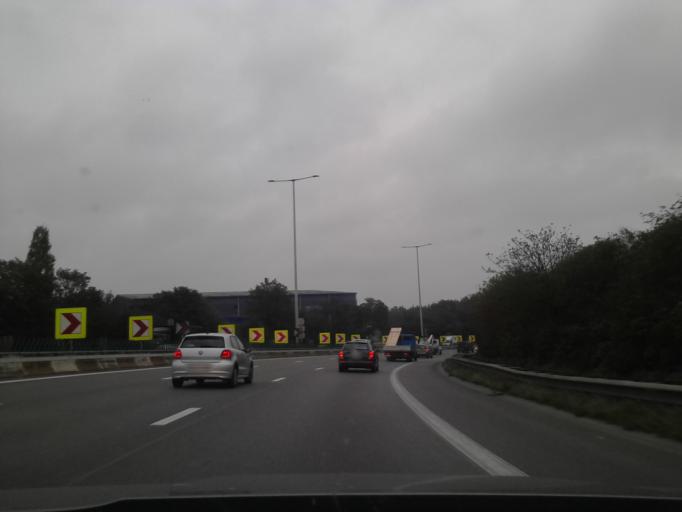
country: BE
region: Flanders
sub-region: Provincie Vlaams-Brabant
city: Drogenbos
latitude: 50.8016
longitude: 4.3068
